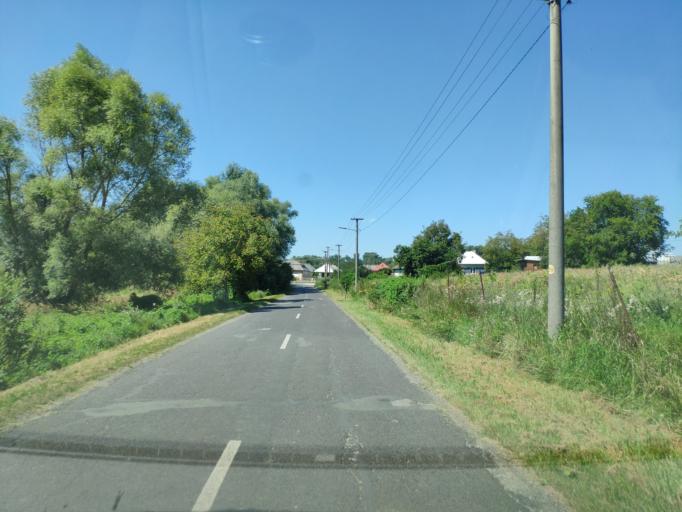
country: SK
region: Kosicky
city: Cierna nad Tisou
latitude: 48.5550
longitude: 21.9545
